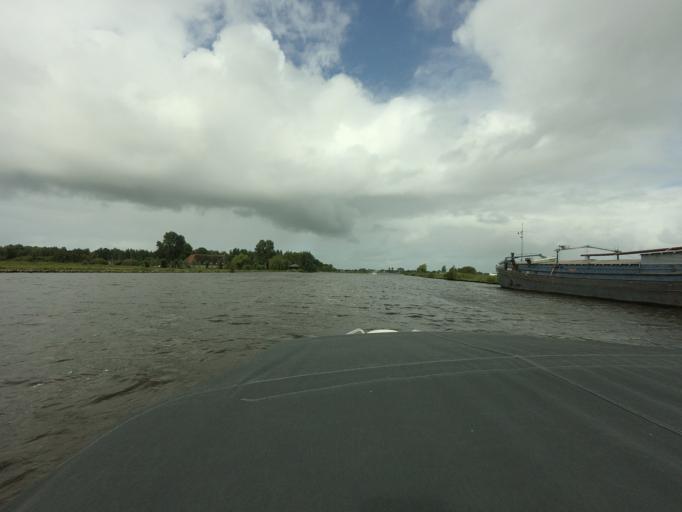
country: NL
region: Friesland
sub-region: Gemeente Boarnsterhim
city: Warten
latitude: 53.1376
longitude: 5.9158
